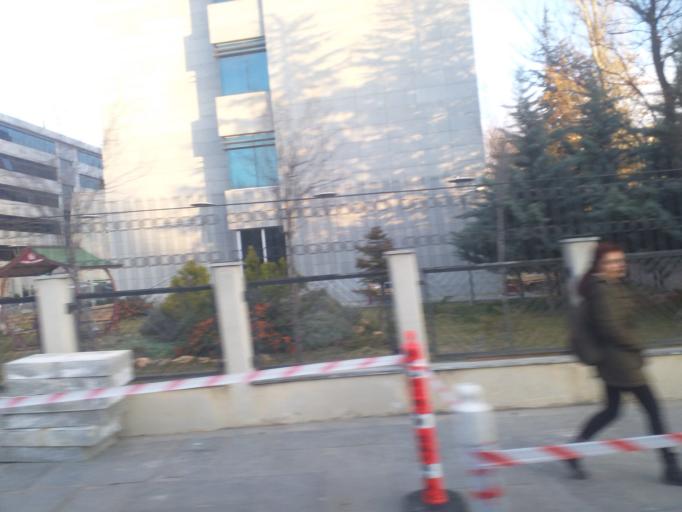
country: TR
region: Ankara
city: Ankara
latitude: 39.9402
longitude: 32.8248
